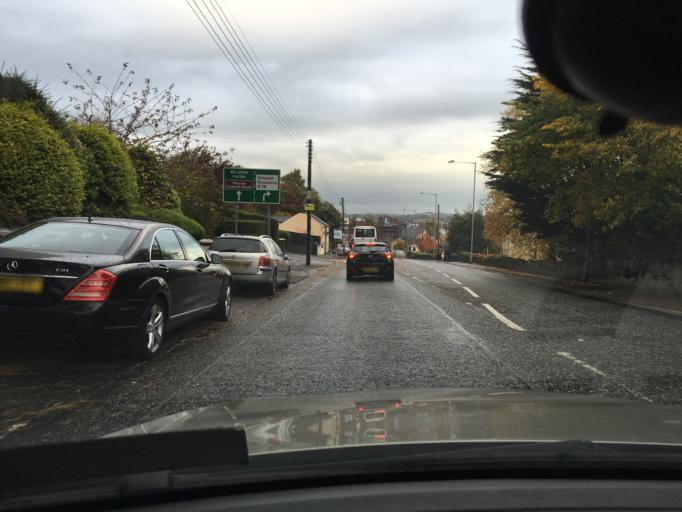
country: GB
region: Northern Ireland
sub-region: Newry and Mourne District
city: Newry
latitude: 54.1672
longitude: -6.3437
